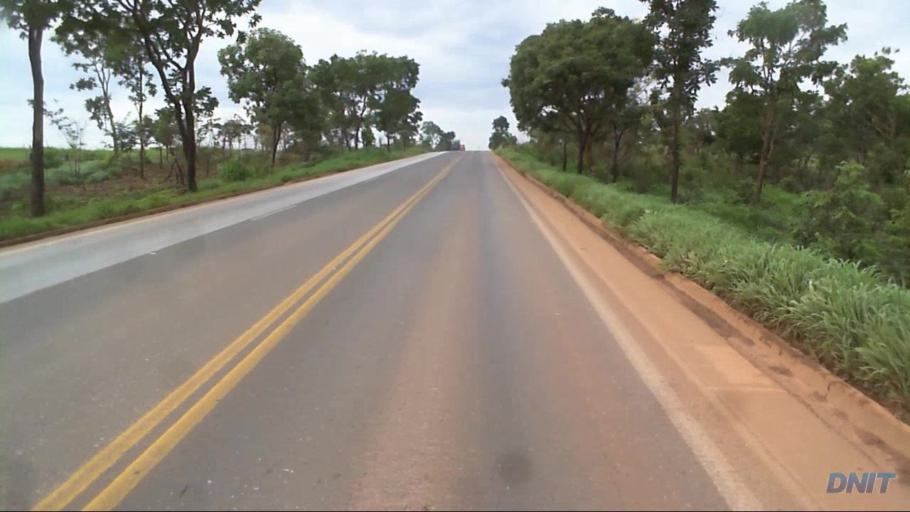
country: BR
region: Goias
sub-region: Uruacu
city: Uruacu
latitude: -14.5819
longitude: -49.1599
